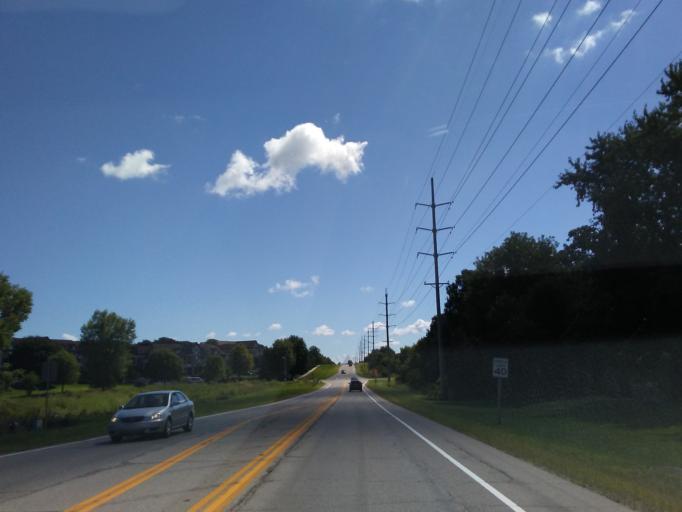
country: US
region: Wisconsin
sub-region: Dane County
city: Verona
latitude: 43.0158
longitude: -89.5141
